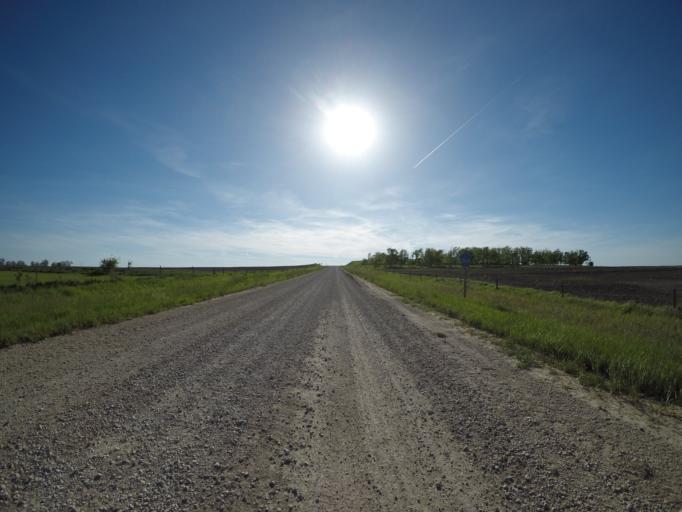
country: US
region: Kansas
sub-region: Clay County
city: Clay Center
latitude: 39.5099
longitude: -97.0717
